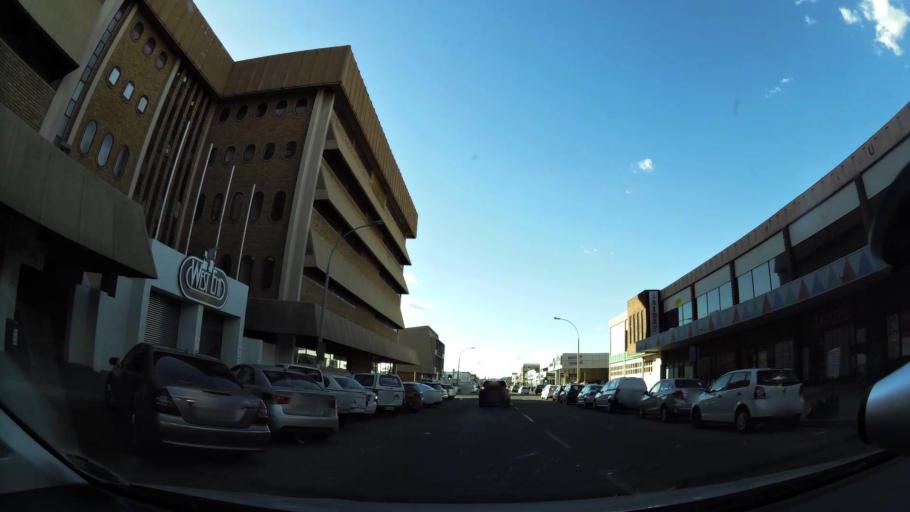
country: ZA
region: North-West
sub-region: Dr Kenneth Kaunda District Municipality
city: Klerksdorp
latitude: -26.8682
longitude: 26.6677
